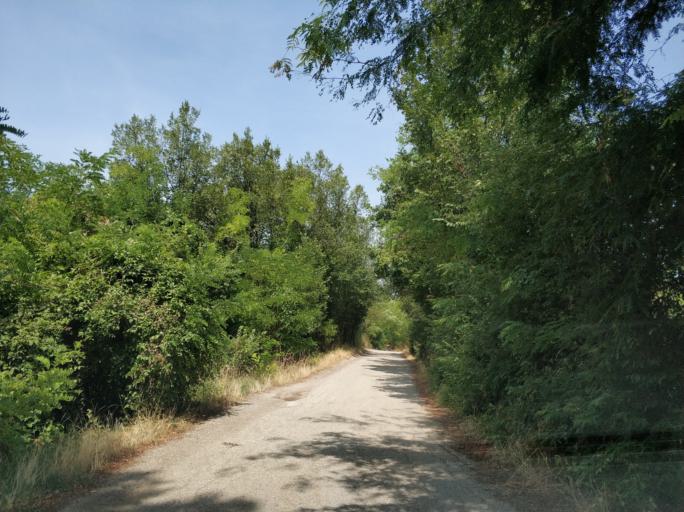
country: IT
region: Veneto
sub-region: Provincia di Padova
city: Arqua Petrarca
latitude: 45.2827
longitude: 11.7053
